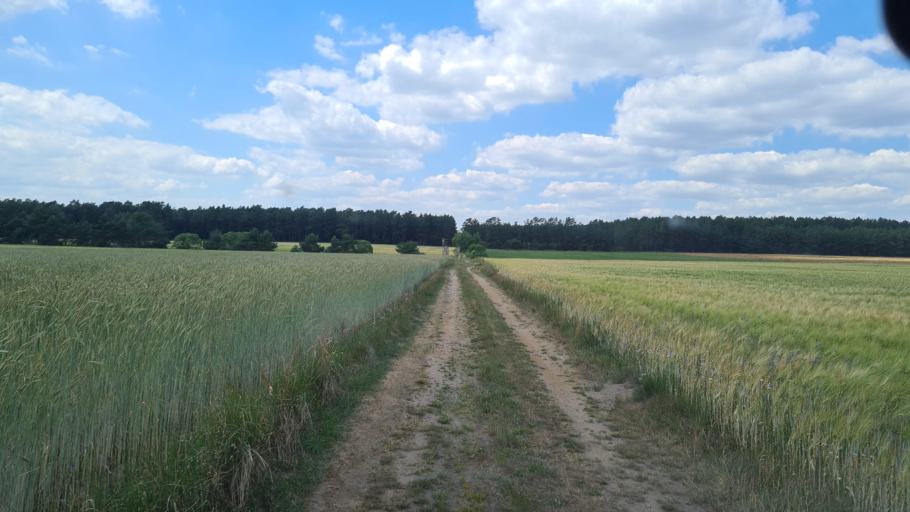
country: DE
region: Brandenburg
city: Sallgast
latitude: 51.6532
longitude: 13.8161
